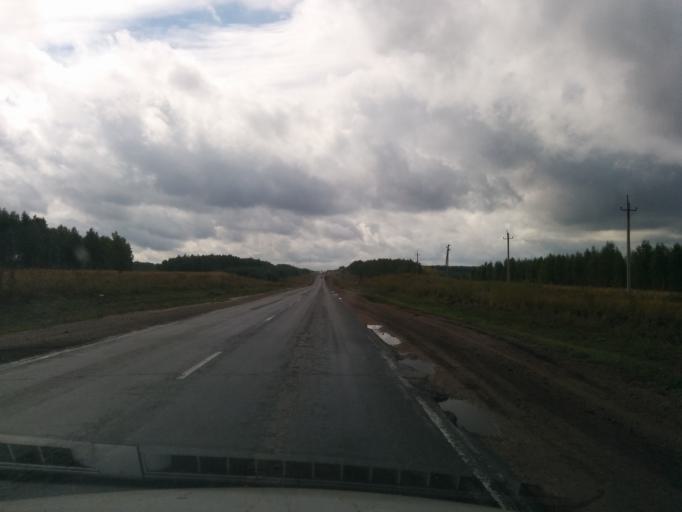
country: RU
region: Tatarstan
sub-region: Bugul'minskiy Rayon
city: Bugul'ma
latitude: 54.2618
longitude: 52.9197
